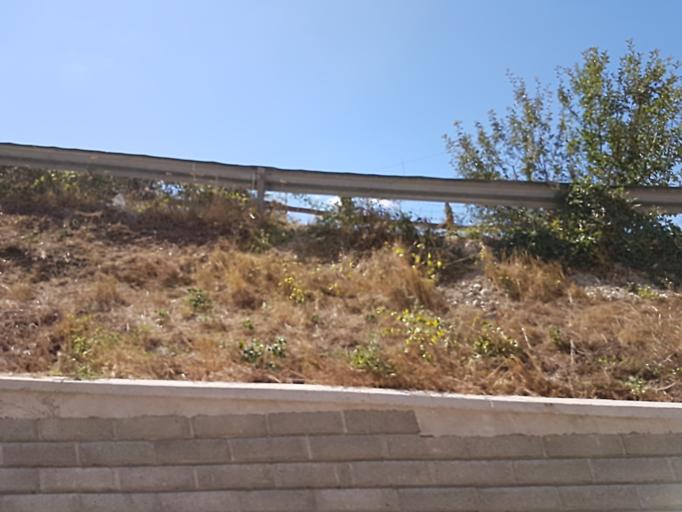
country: IT
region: Latium
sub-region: Provincia di Rieti
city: Accumoli
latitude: 42.6956
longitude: 13.2561
